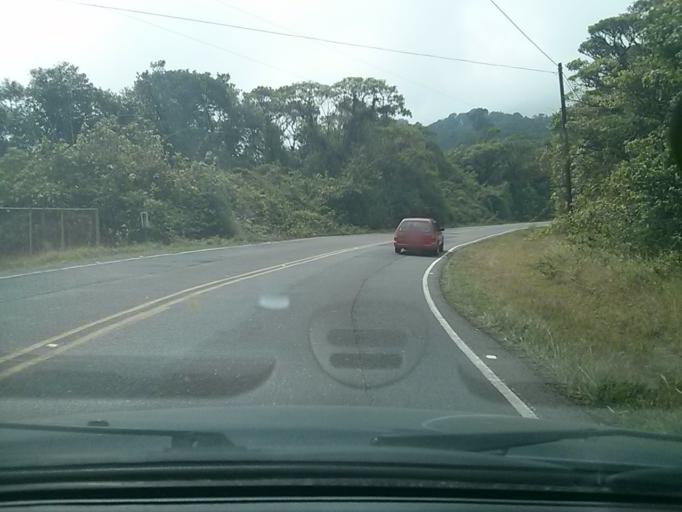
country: CR
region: Cartago
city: Tobosi
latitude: 9.7418
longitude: -83.9650
